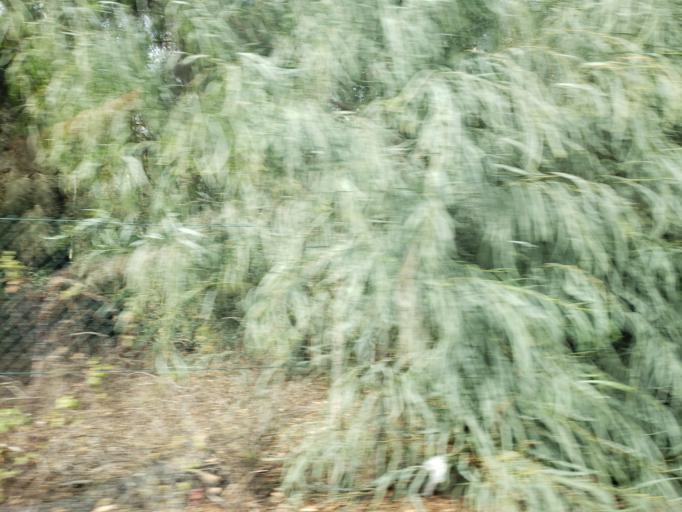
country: PT
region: Faro
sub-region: Portimao
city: Alvor
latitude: 37.1654
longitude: -8.5777
